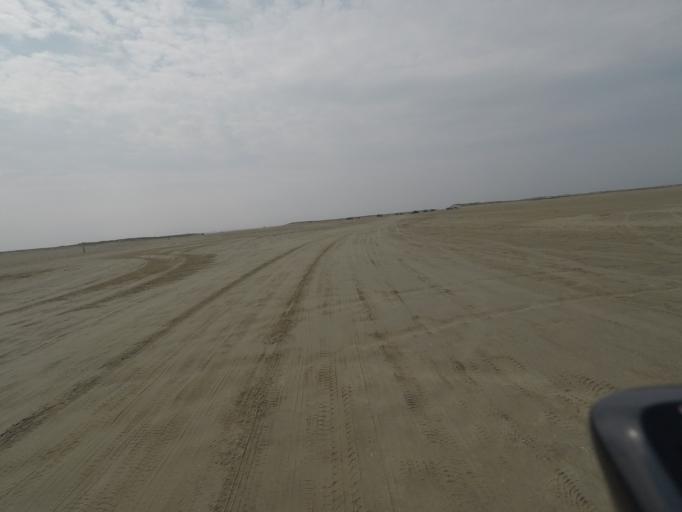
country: DE
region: Schleswig-Holstein
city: List
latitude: 55.0747
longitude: 8.5009
